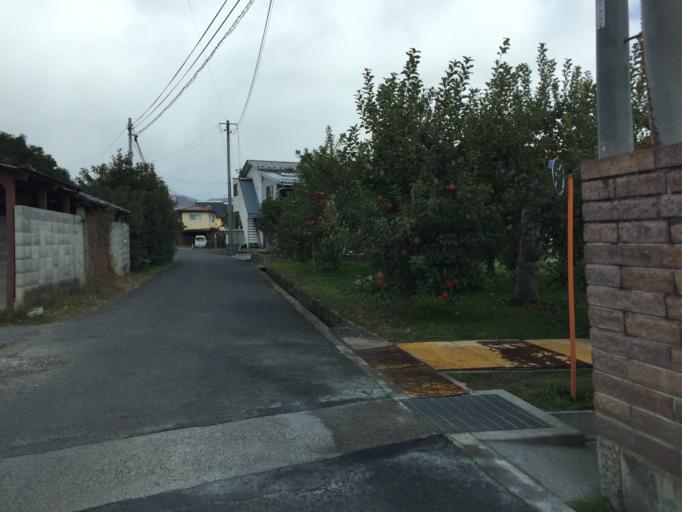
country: JP
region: Fukushima
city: Fukushima-shi
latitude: 37.8102
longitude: 140.4345
